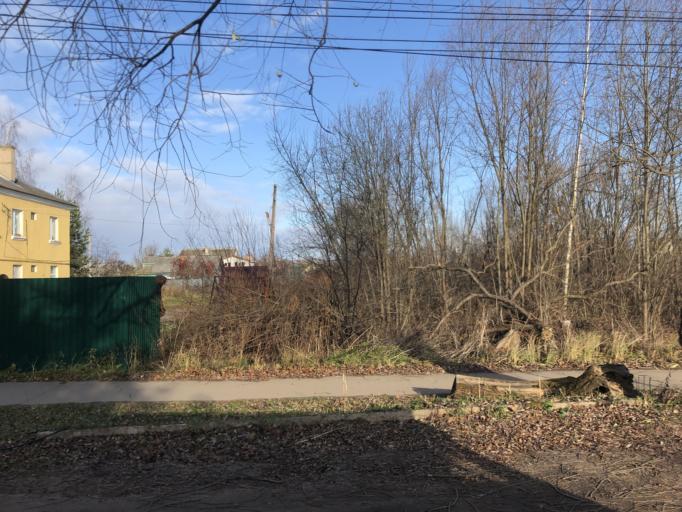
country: RU
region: Tverskaya
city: Rzhev
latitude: 56.2635
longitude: 34.3121
